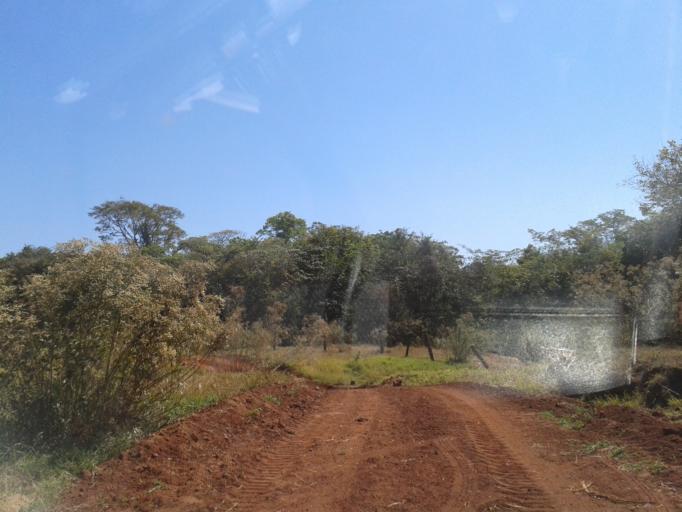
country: BR
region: Minas Gerais
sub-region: Santa Vitoria
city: Santa Vitoria
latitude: -19.0777
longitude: -50.0290
